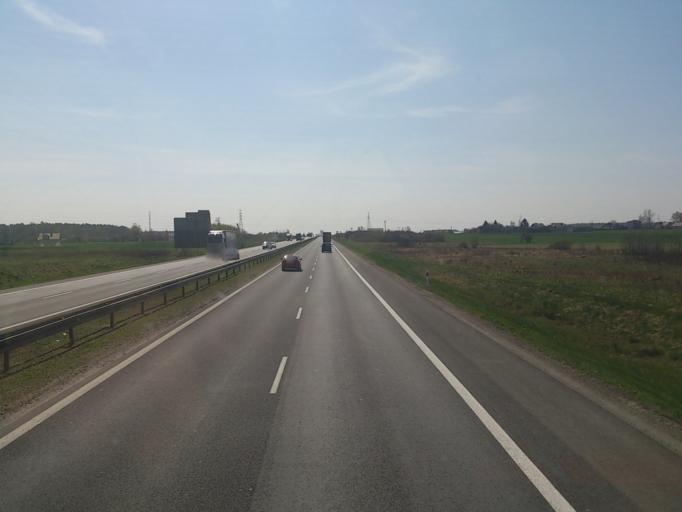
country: PL
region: Lodz Voivodeship
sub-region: Piotrkow Trybunalski
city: Piotrkow Trybunalski
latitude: 51.4026
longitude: 19.6323
